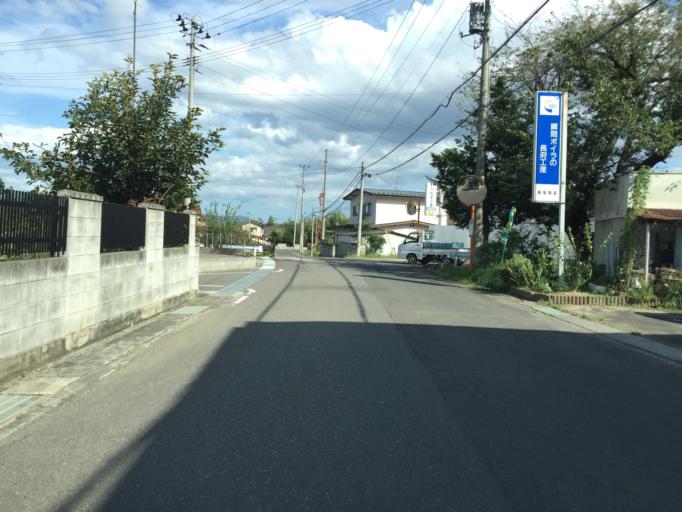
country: JP
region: Fukushima
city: Fukushima-shi
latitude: 37.7882
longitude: 140.4020
